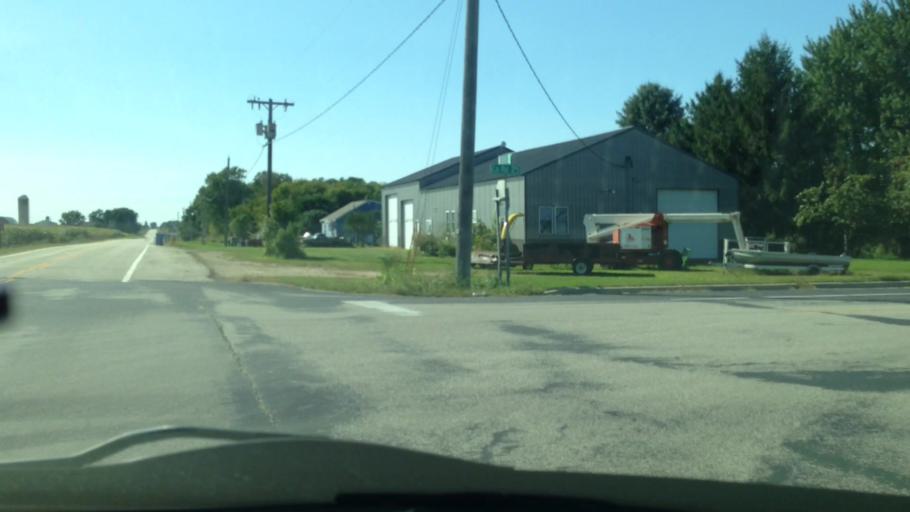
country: US
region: Minnesota
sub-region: Winona County
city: Lewiston
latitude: 43.9405
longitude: -91.7900
